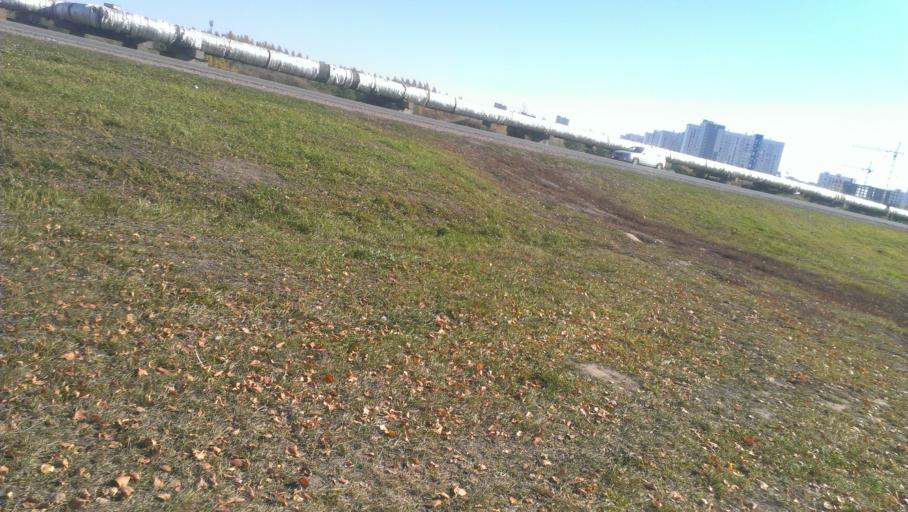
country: RU
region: Altai Krai
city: Novosilikatnyy
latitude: 53.3442
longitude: 83.6346
